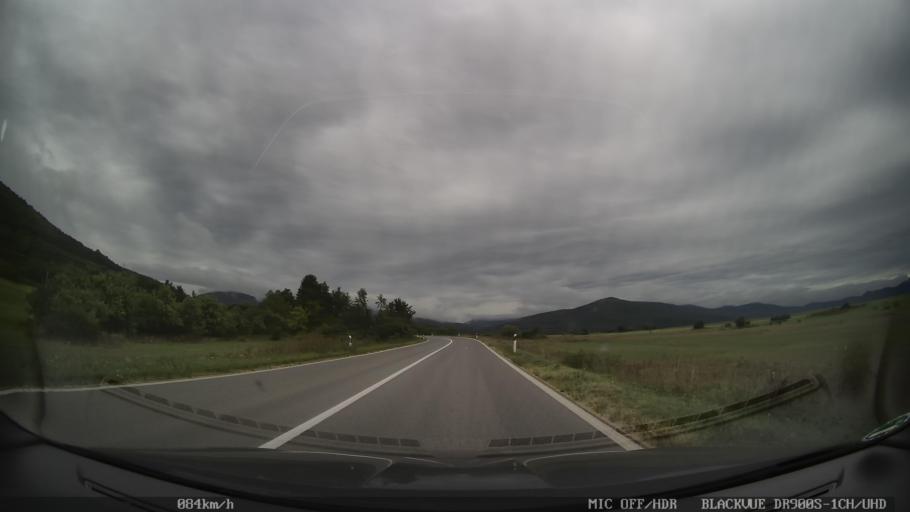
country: HR
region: Licko-Senjska
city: Otocac
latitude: 44.8606
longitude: 15.3004
